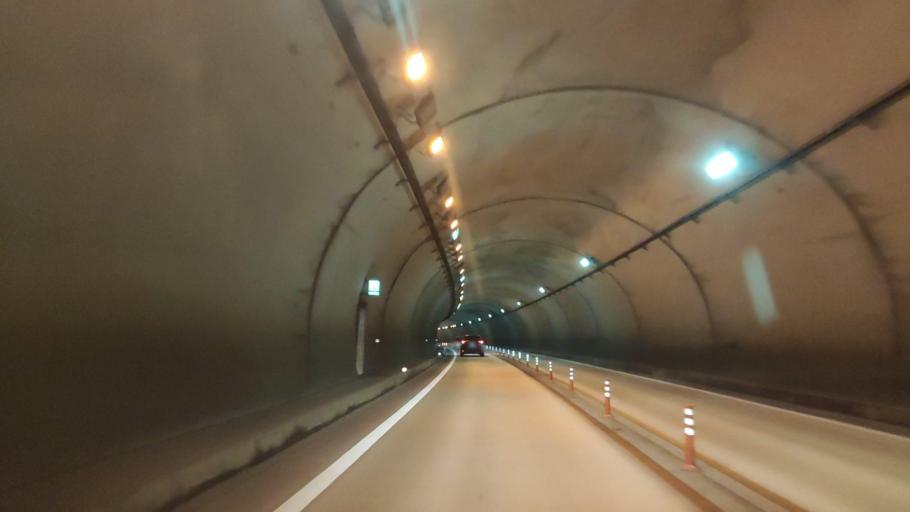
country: JP
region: Hiroshima
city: Innoshima
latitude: 34.2933
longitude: 133.1435
